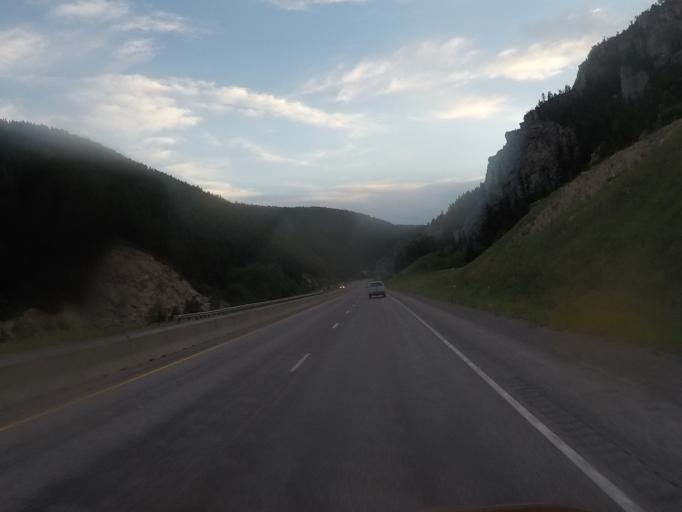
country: US
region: Montana
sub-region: Gallatin County
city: Bozeman
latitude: 45.6427
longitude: -110.9025
